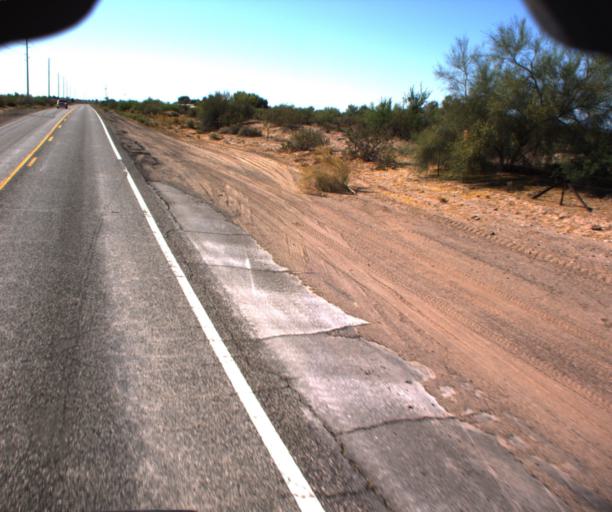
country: US
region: Arizona
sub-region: La Paz County
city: Cienega Springs
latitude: 33.9503
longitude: -114.0208
